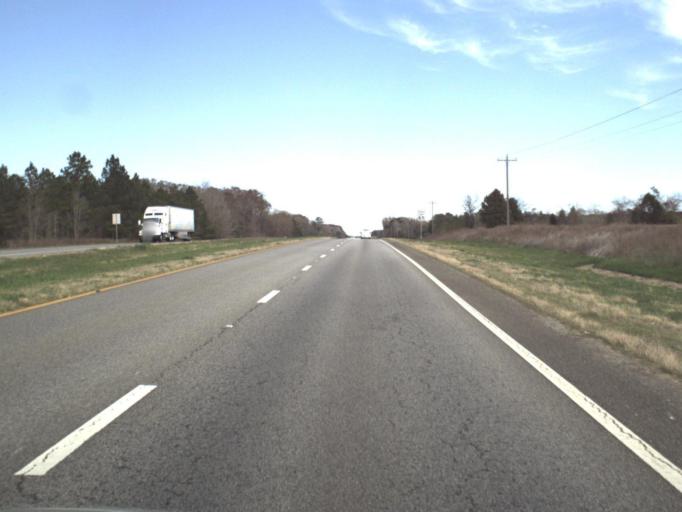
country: US
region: Florida
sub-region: Jackson County
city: Marianna
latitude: 30.8138
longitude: -85.3721
